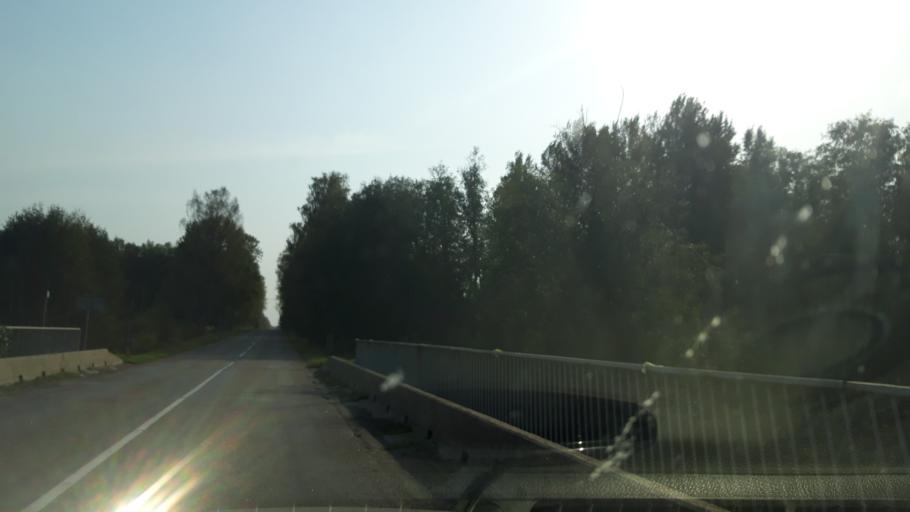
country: LV
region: Burtnieki
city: Matisi
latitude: 57.6548
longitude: 25.2312
